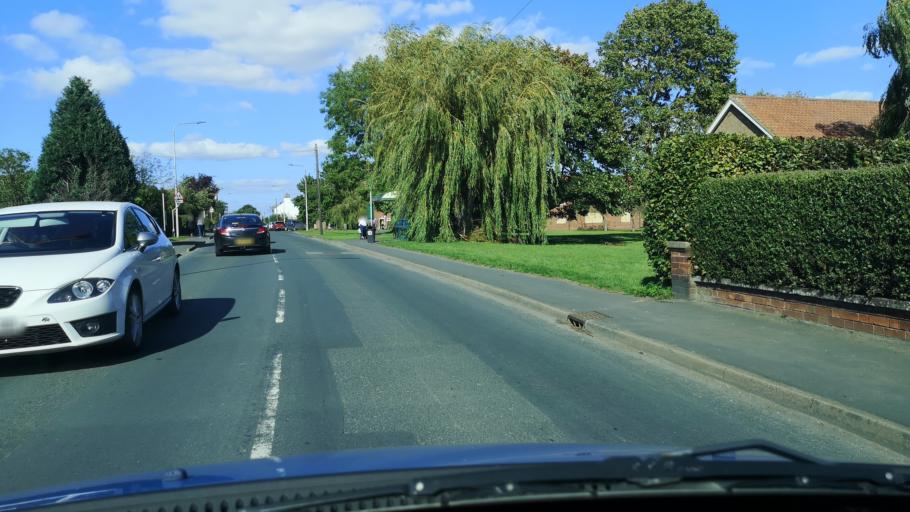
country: GB
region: England
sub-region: North Lincolnshire
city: Belton
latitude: 53.5533
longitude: -0.8164
